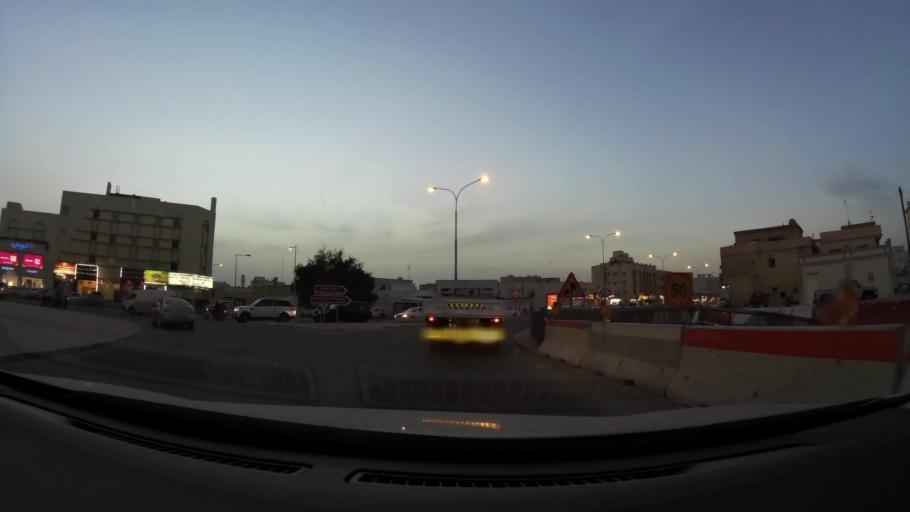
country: QA
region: Al Wakrah
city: Al Wakrah
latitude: 25.1612
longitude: 51.5986
